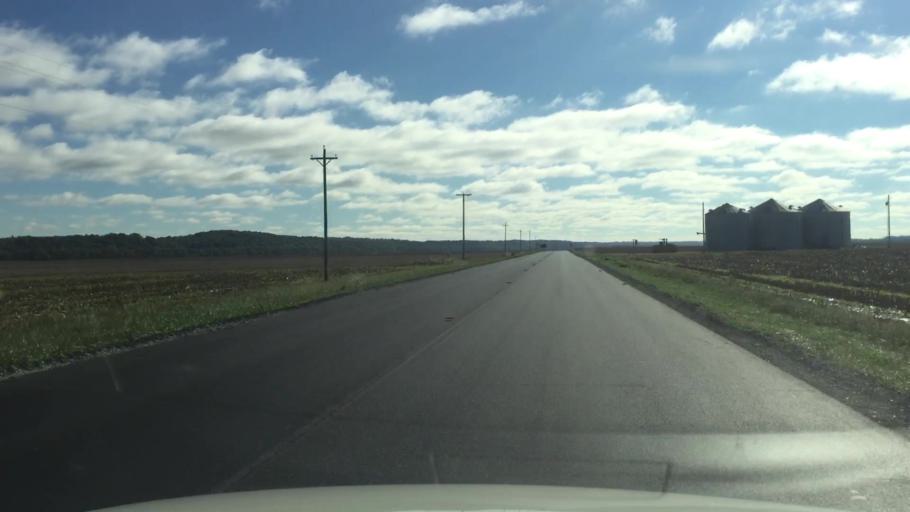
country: US
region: Missouri
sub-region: Howard County
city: New Franklin
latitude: 39.0016
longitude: -92.6850
